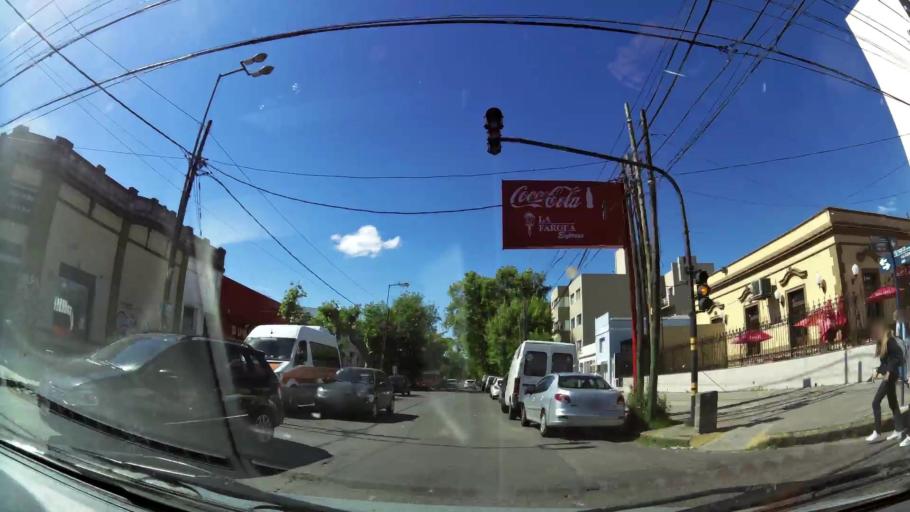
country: AR
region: Buenos Aires
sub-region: Partido de Lomas de Zamora
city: Lomas de Zamora
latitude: -34.7596
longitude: -58.4085
